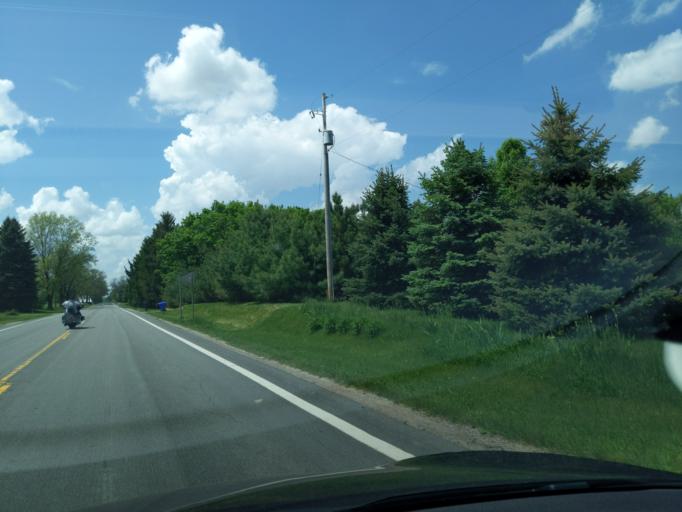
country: US
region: Michigan
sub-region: Ingham County
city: Stockbridge
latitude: 42.5063
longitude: -84.1494
